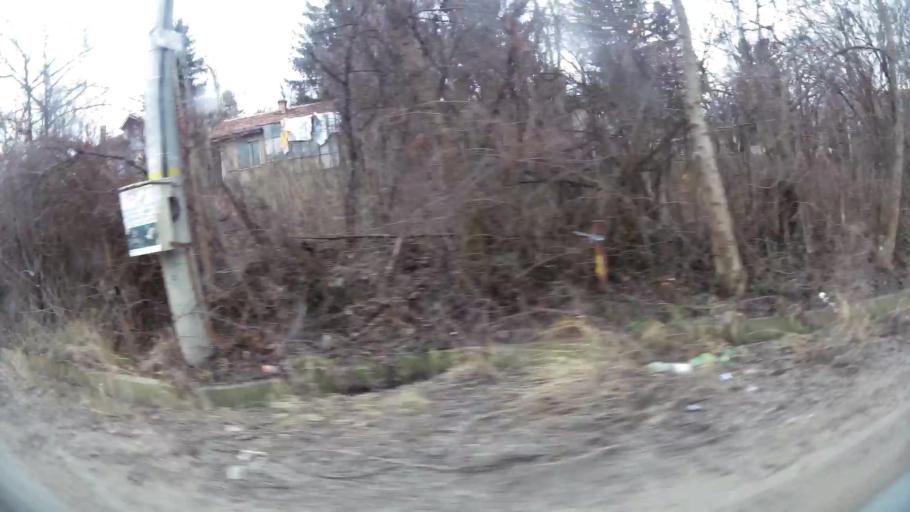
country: BG
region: Sofia-Capital
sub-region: Stolichna Obshtina
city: Sofia
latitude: 42.6177
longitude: 23.3601
